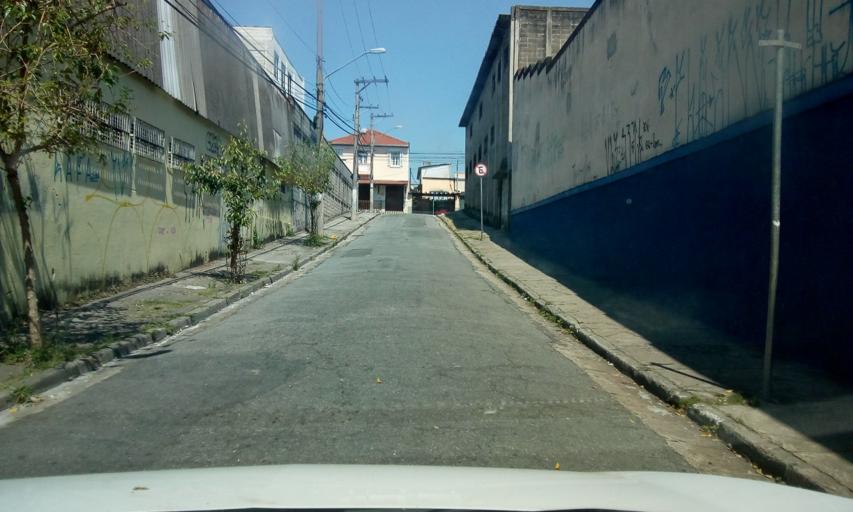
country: BR
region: Sao Paulo
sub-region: Osasco
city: Osasco
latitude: -23.5125
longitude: -46.7199
